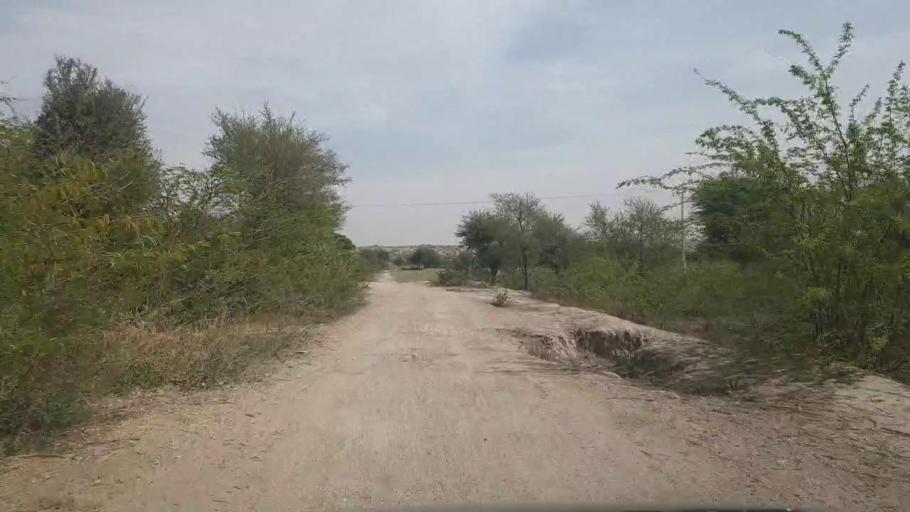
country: PK
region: Sindh
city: Kunri
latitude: 25.1917
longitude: 69.7020
